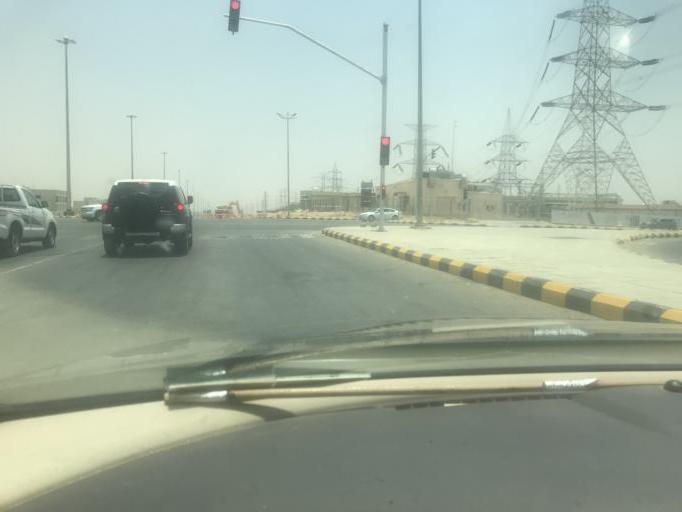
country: SA
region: Ar Riyad
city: Riyadh
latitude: 24.8155
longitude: 46.7311
